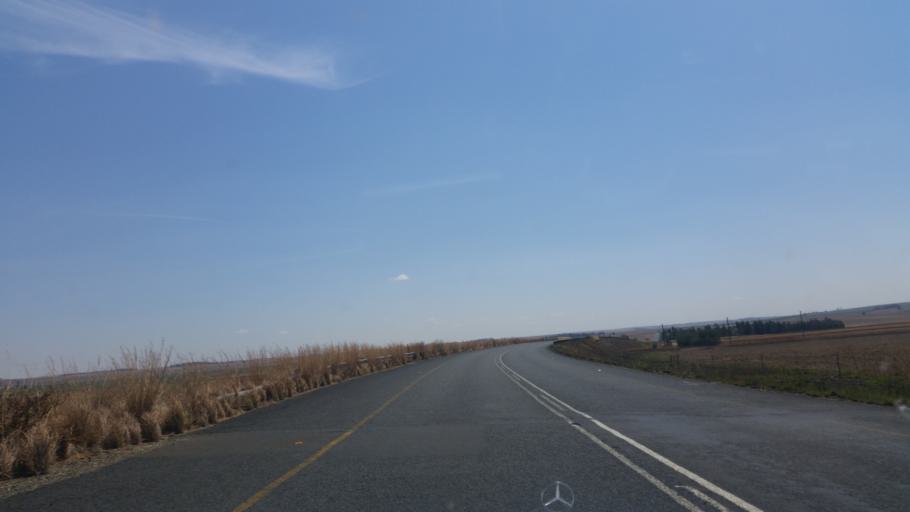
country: ZA
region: Orange Free State
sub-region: Thabo Mofutsanyana District Municipality
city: Phuthaditjhaba
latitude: -28.2061
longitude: 28.6888
